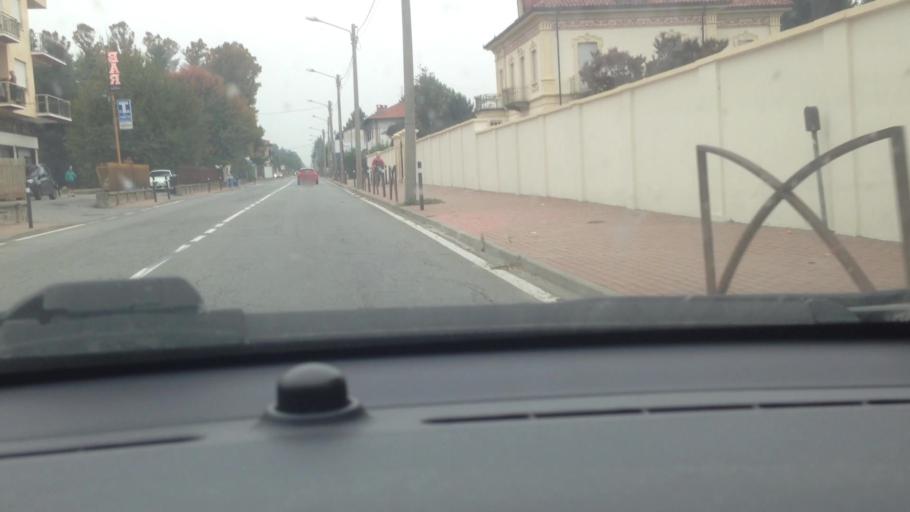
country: IT
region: Piedmont
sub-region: Provincia di Torino
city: Rivarolo Canavese
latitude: 45.3372
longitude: 7.7184
